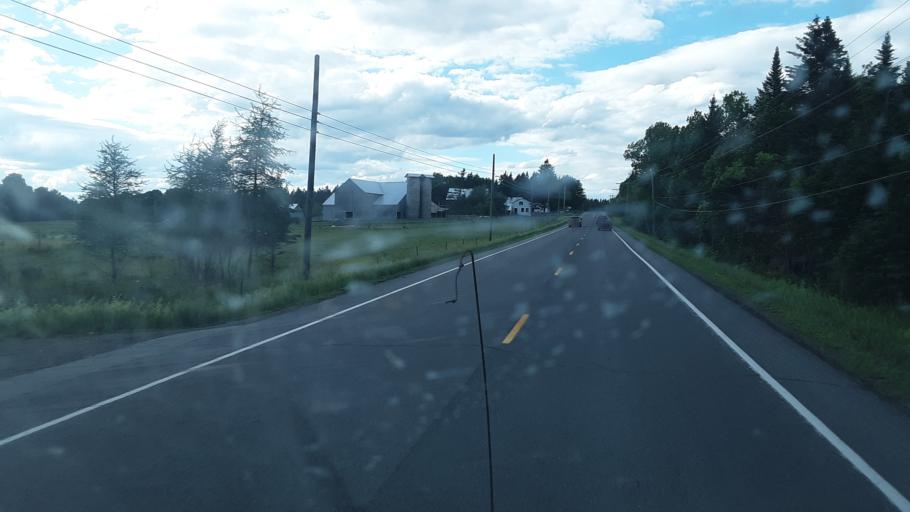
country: US
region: Maine
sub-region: Penobscot County
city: Patten
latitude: 45.9355
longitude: -68.4494
